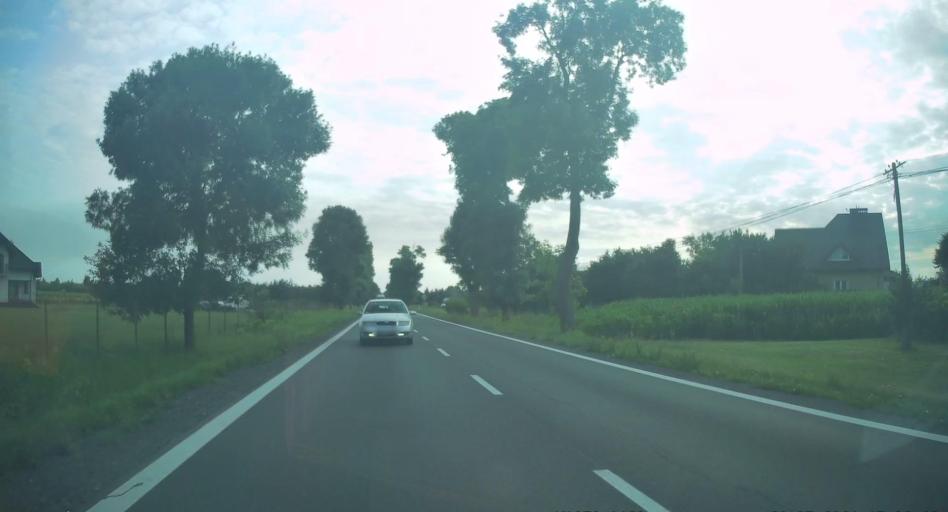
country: PL
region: Silesian Voivodeship
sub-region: Powiat czestochowski
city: Borowno
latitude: 50.9034
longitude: 19.2916
